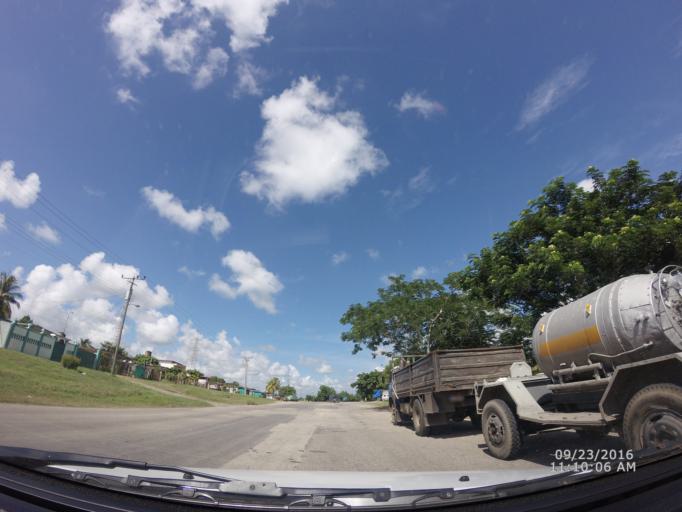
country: CU
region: La Habana
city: Arroyo Naranjo
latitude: 23.0195
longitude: -82.2533
